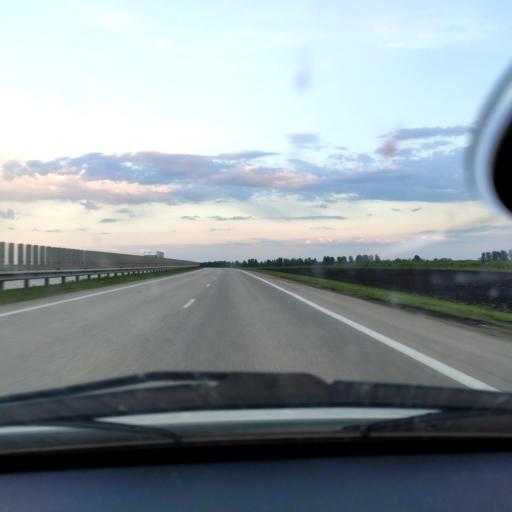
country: RU
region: Bashkortostan
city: Kushnarenkovo
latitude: 55.0904
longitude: 55.2510
